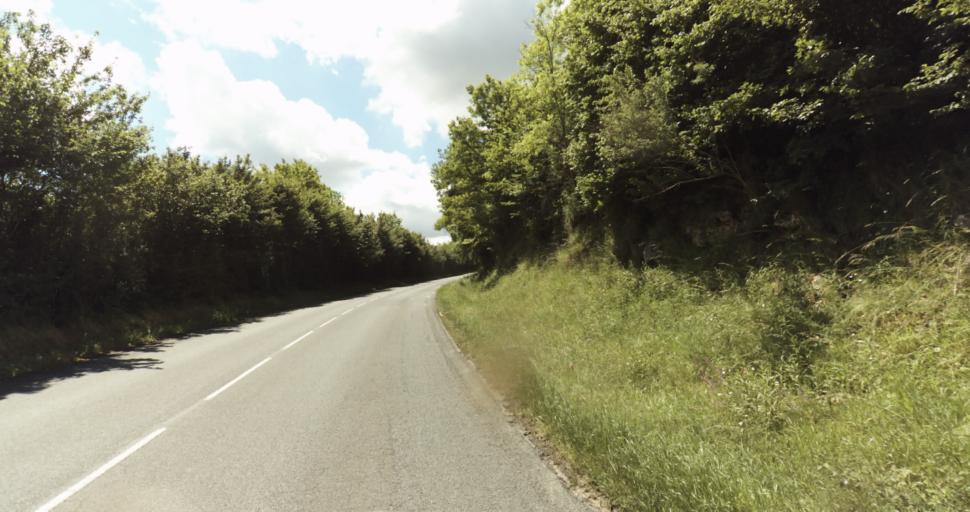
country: FR
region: Aquitaine
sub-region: Departement de la Dordogne
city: Beaumont-du-Perigord
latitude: 44.7805
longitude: 0.7669
